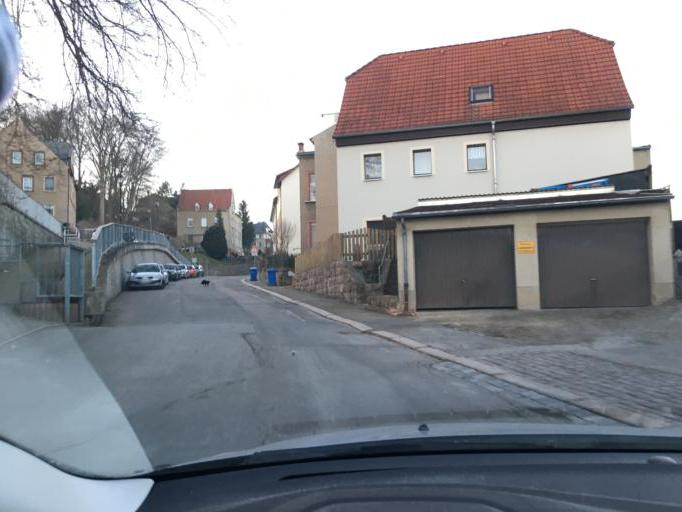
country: DE
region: Saxony
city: Lunzenau
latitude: 50.9606
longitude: 12.7554
